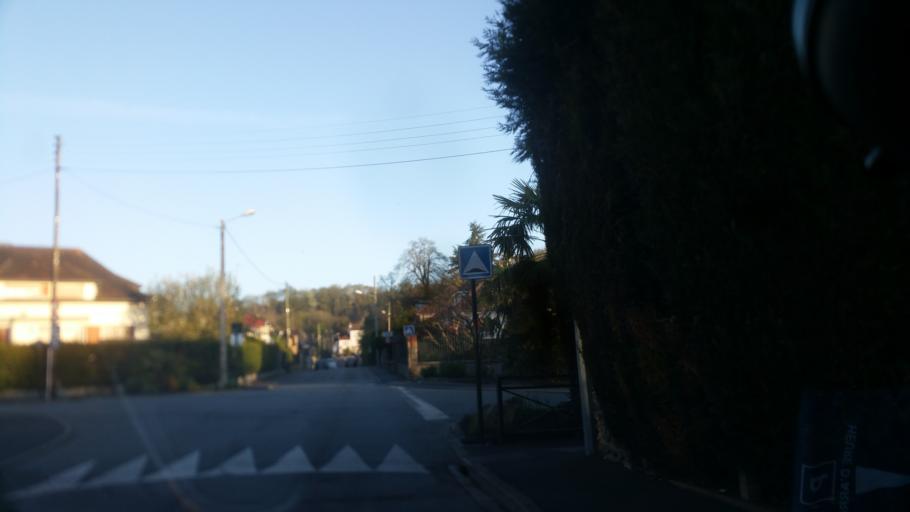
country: FR
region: Ile-de-France
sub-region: Departement de l'Essonne
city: Limours
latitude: 48.6462
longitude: 2.0728
